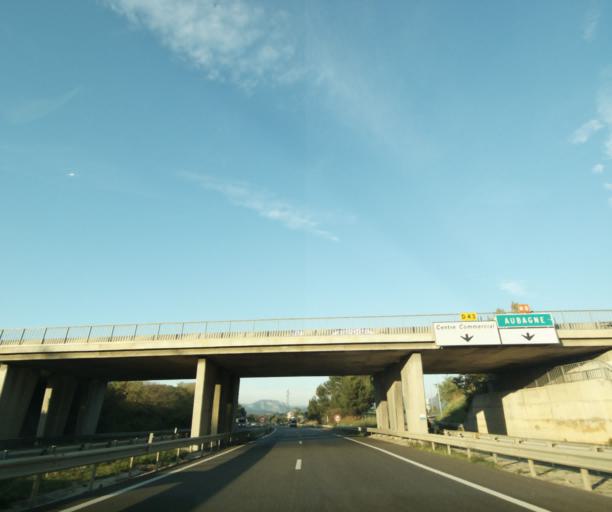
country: FR
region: Provence-Alpes-Cote d'Azur
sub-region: Departement des Bouches-du-Rhone
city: Aubagne
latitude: 43.2863
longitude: 5.5861
